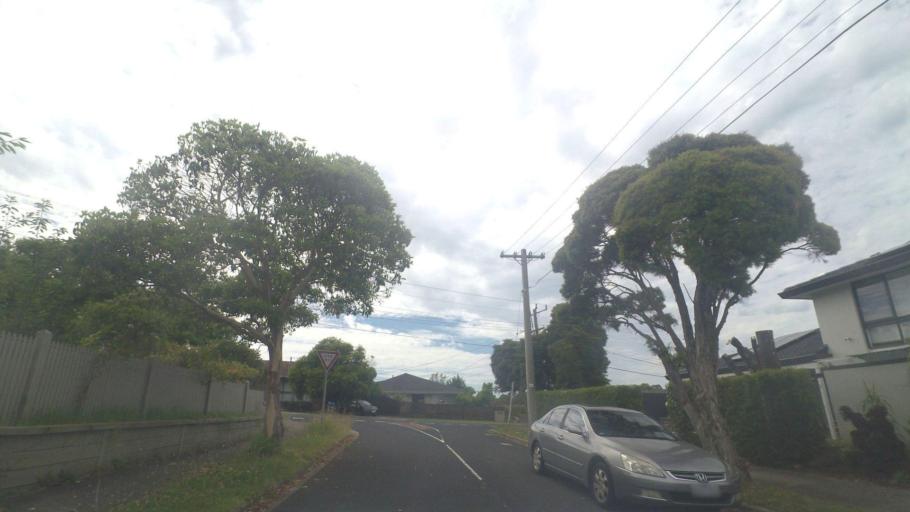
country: AU
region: Victoria
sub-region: Banyule
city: Viewbank
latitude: -37.7382
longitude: 145.0907
